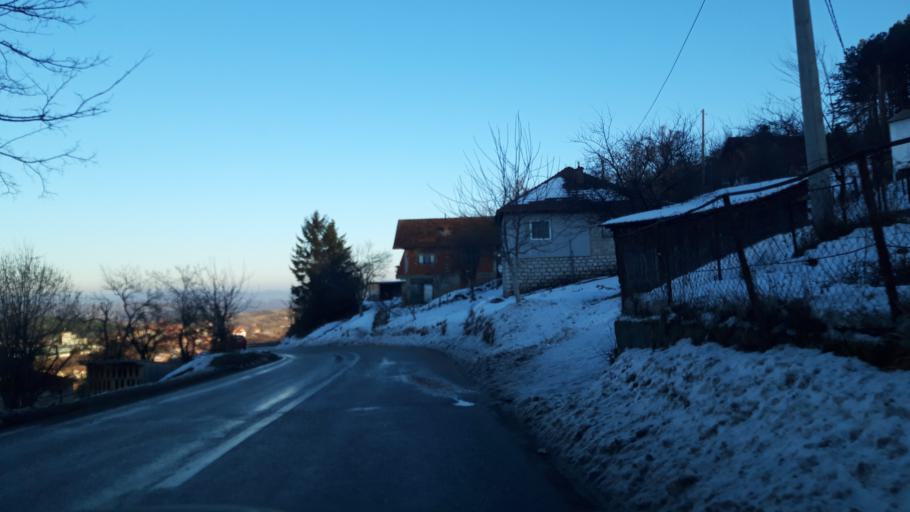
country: BA
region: Republika Srpska
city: Vlasenica
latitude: 44.1781
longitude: 18.9465
